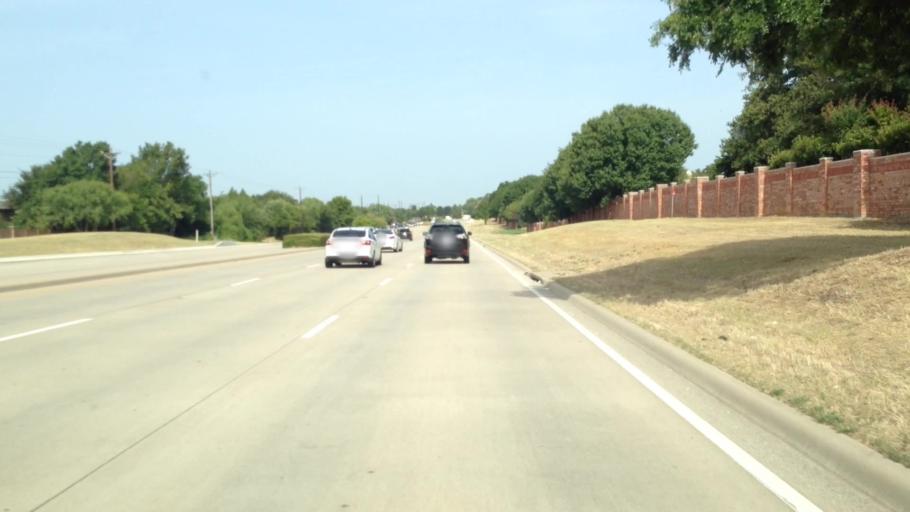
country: US
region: Texas
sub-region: Denton County
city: Lewisville
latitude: 33.0101
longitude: -97.0376
